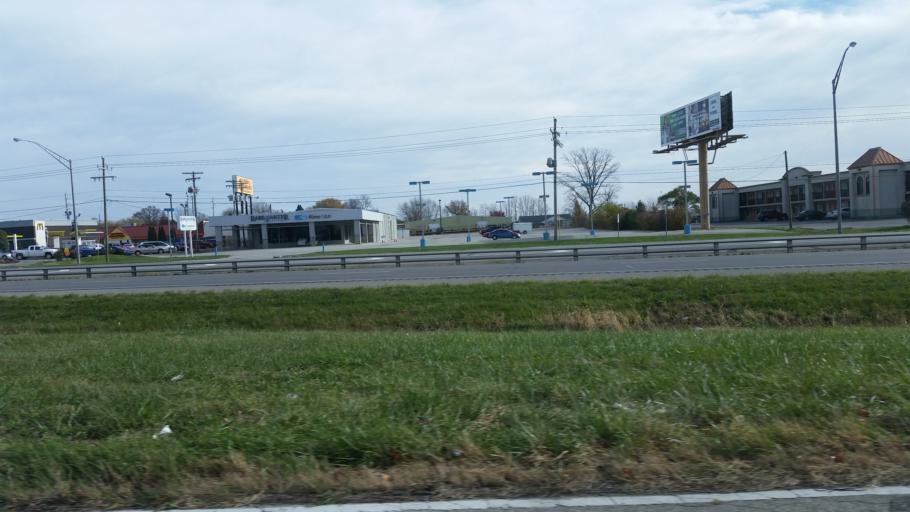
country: US
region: Indiana
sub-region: Howard County
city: Indian Heights
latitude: 40.4396
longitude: -86.1271
